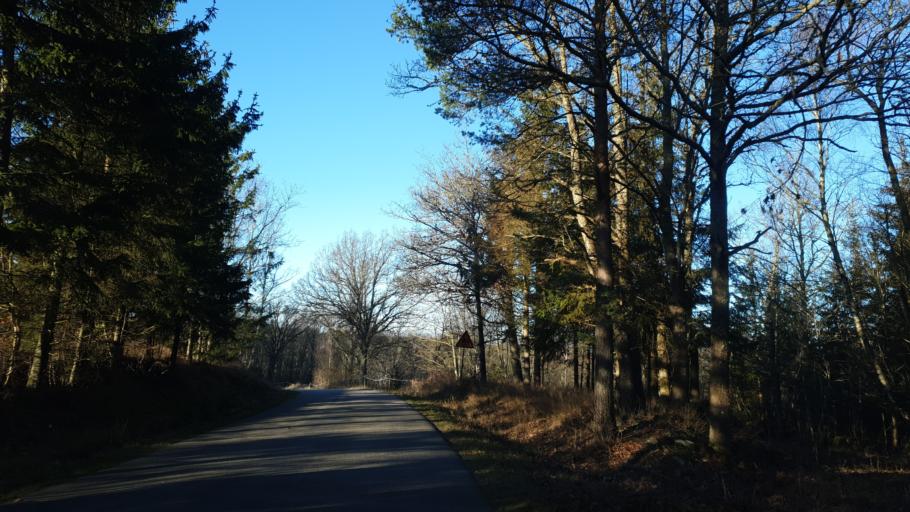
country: SE
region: Blekinge
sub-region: Karlskrona Kommun
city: Nattraby
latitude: 56.2667
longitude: 15.4710
